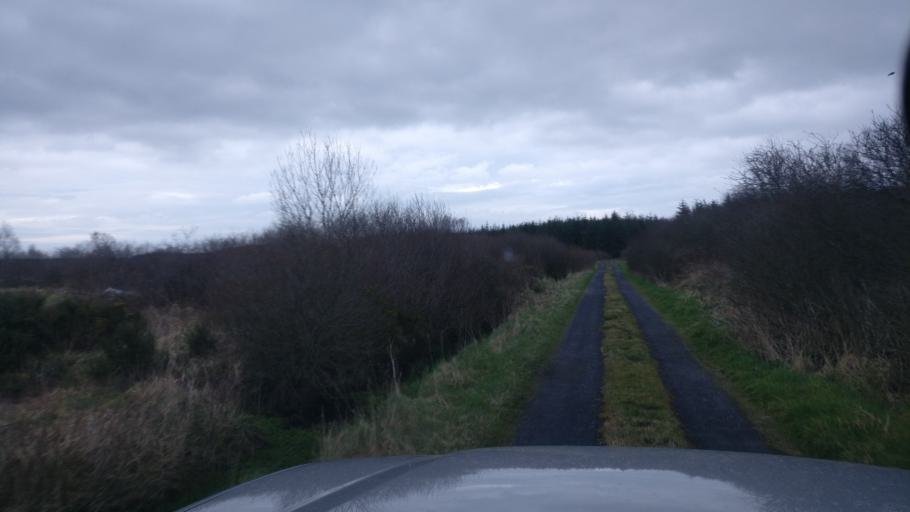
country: IE
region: Connaught
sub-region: County Galway
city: Loughrea
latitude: 53.2717
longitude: -8.4658
